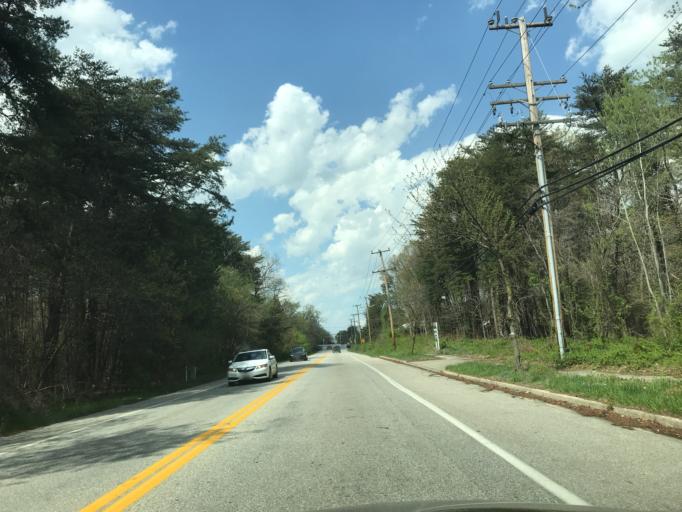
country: US
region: Maryland
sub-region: Anne Arundel County
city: Ferndale
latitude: 39.1593
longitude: -76.6678
